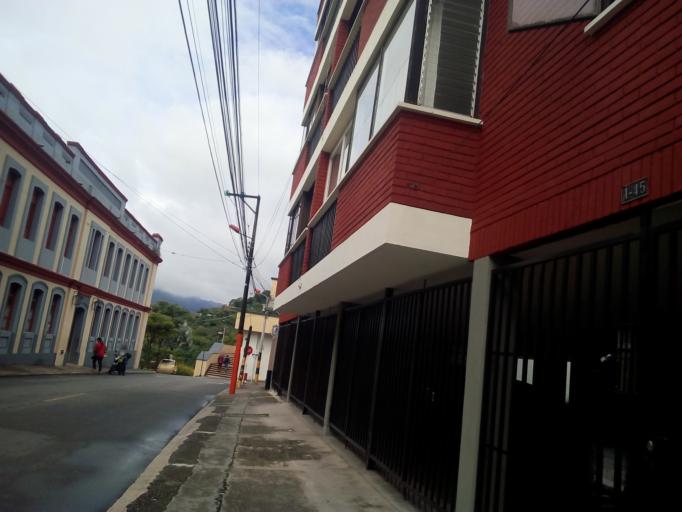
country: CO
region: Tolima
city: Ibague
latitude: 4.4440
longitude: -75.2443
